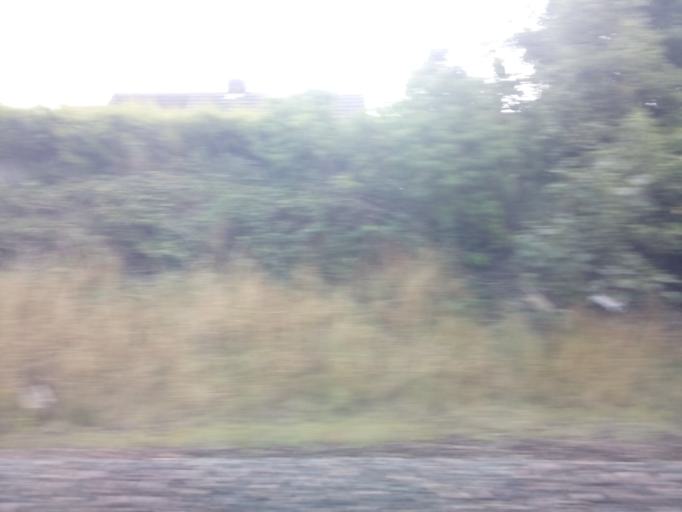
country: GB
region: England
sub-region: County Durham
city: Chester-le-Street
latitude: 54.8480
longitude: -1.5773
